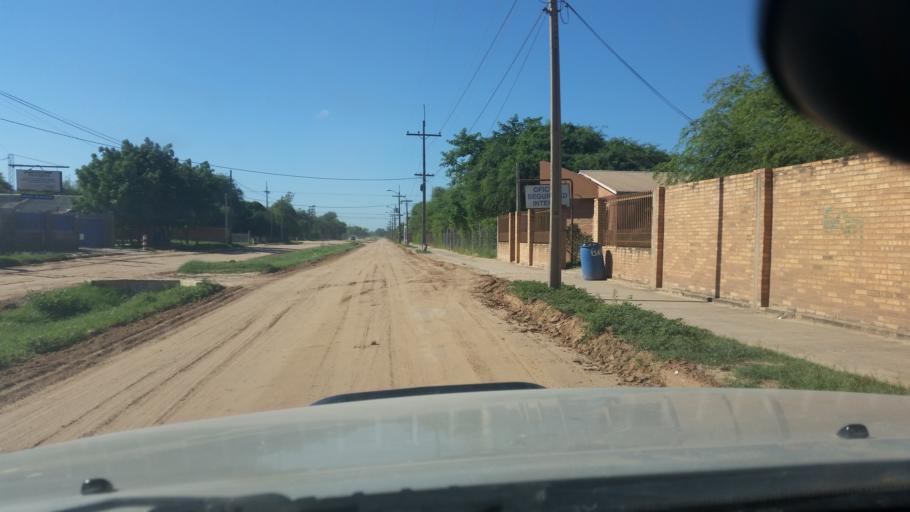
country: PY
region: Boqueron
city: Filadelfia
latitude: -22.3591
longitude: -60.0272
